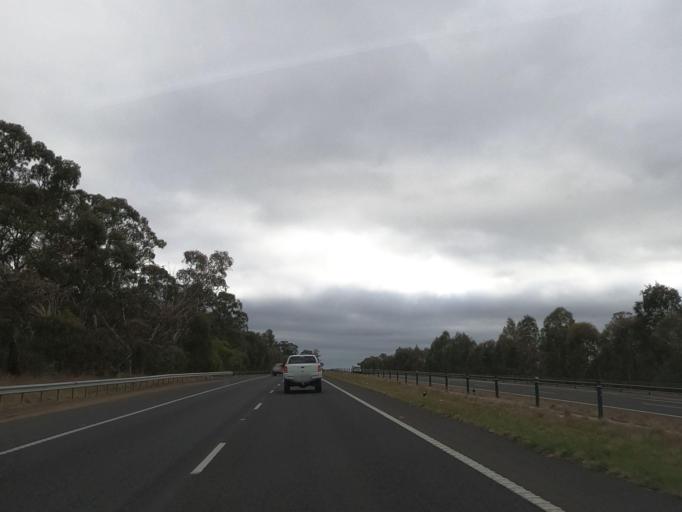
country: AU
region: Victoria
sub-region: Mount Alexander
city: Castlemaine
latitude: -37.0317
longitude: 144.2750
